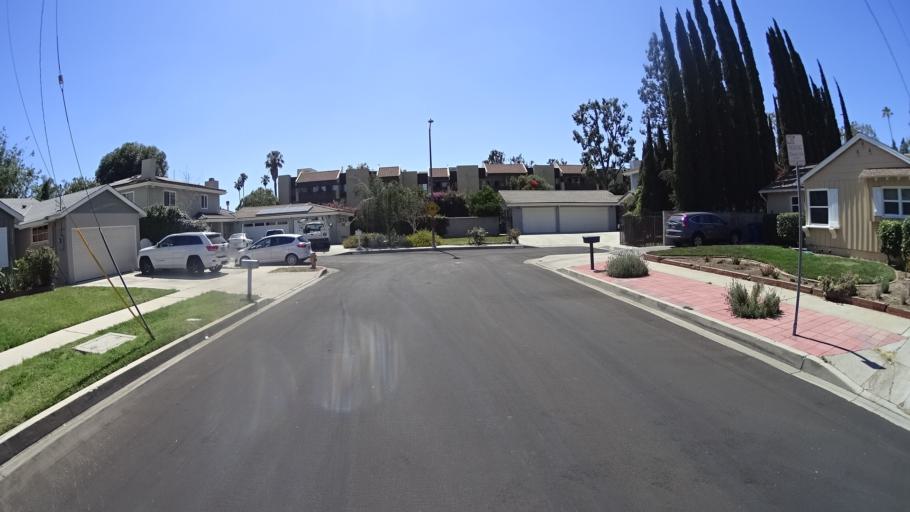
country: US
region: California
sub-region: Los Angeles County
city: Van Nuys
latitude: 34.2000
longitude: -118.4799
